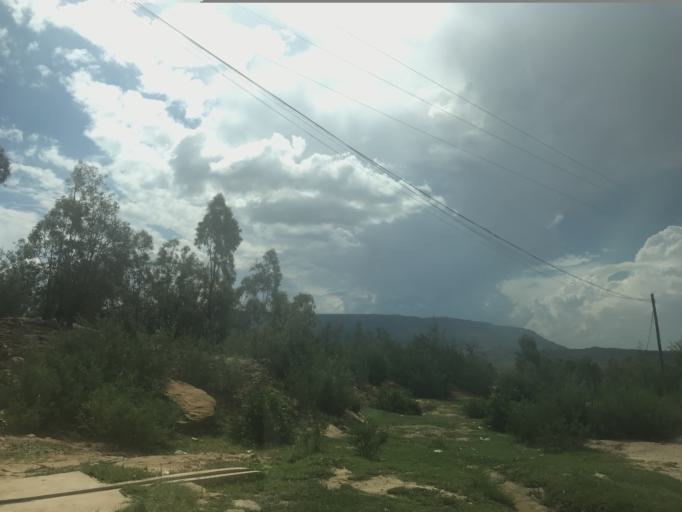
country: LS
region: Maseru
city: Nako
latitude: -29.6300
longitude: 27.5134
